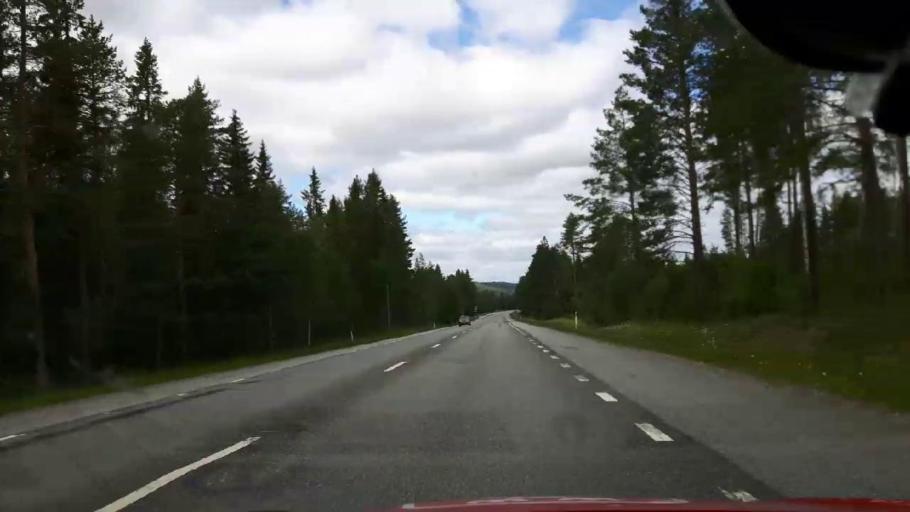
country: SE
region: Jaemtland
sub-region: Braecke Kommun
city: Braecke
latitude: 62.7137
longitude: 15.4663
